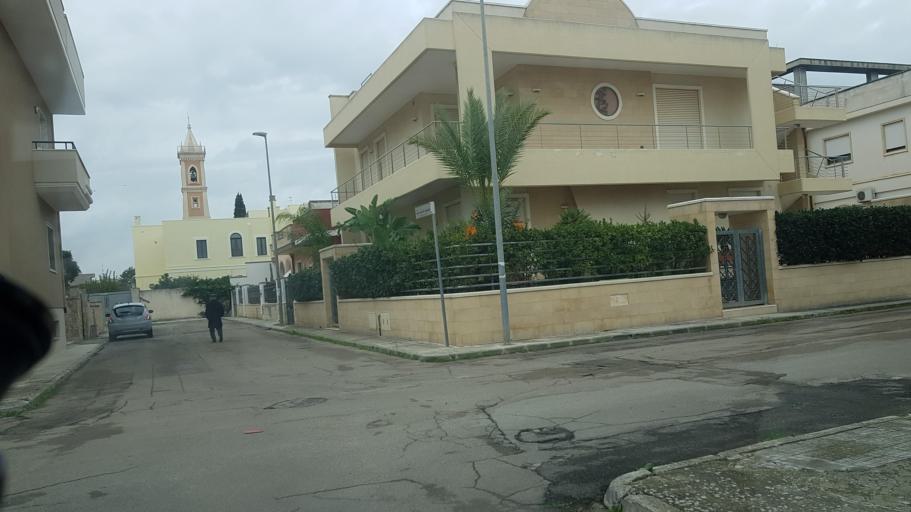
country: IT
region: Apulia
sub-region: Provincia di Lecce
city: Novoli
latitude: 40.3803
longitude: 18.0449
